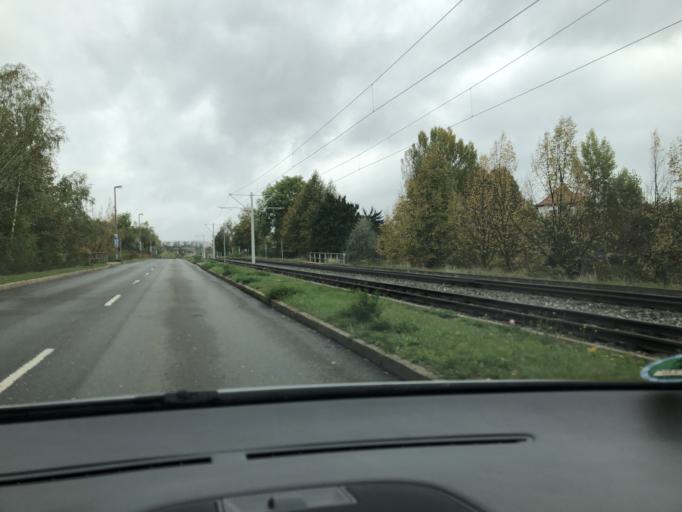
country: DE
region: Thuringia
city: Gera
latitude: 50.9057
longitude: 12.0809
